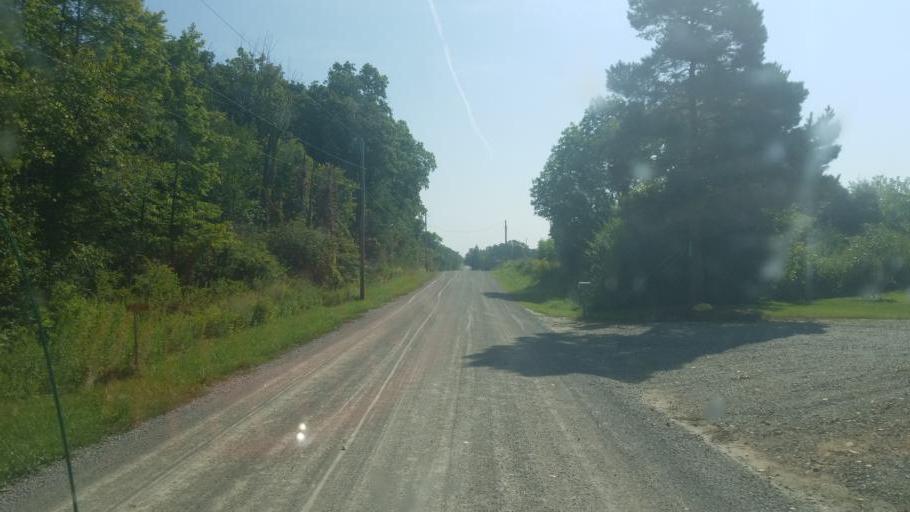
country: US
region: Ohio
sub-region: Wayne County
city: West Salem
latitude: 41.0064
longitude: -82.1249
